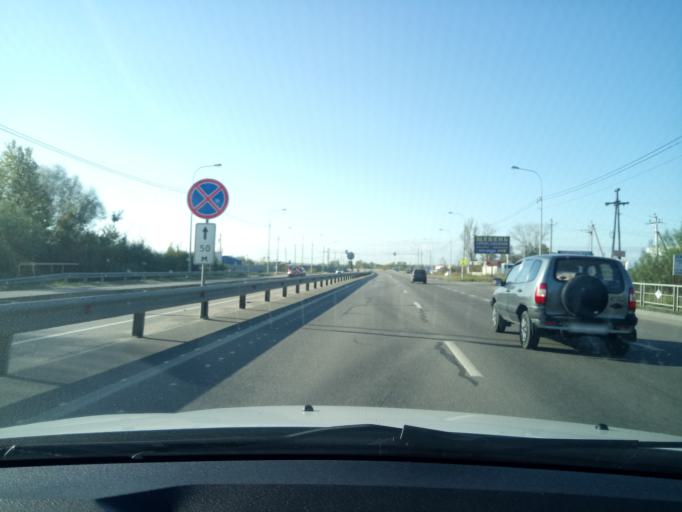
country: RU
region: Nizjnij Novgorod
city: Burevestnik
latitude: 56.1624
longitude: 43.9147
